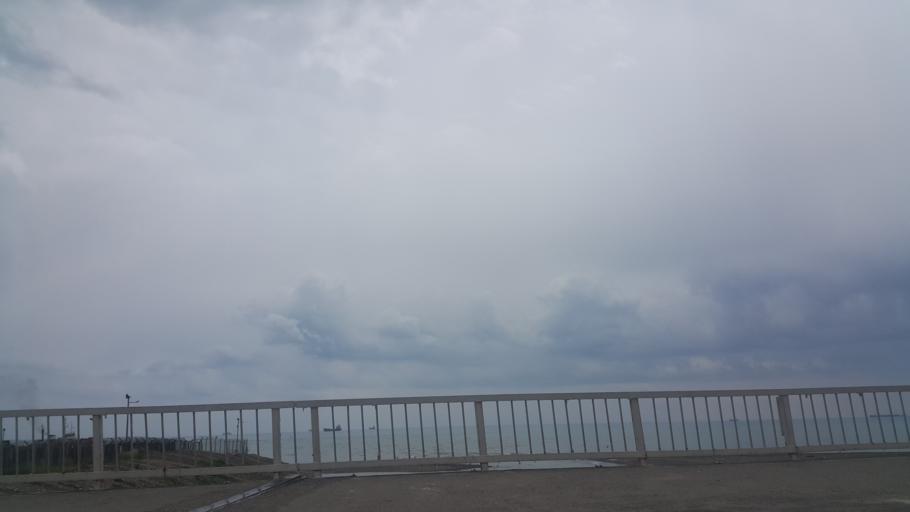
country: TR
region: Mersin
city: Mercin
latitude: 36.7857
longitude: 34.6200
